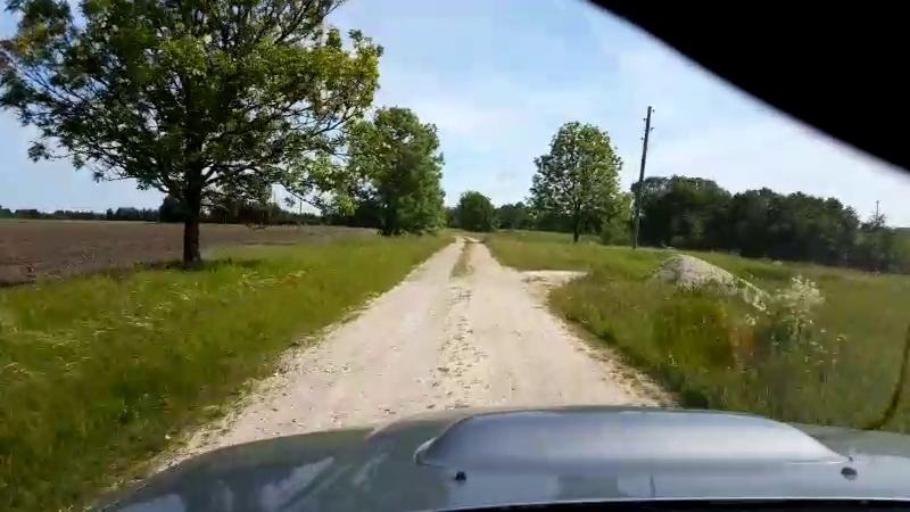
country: EE
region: Paernumaa
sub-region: Sauga vald
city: Sauga
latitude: 58.4946
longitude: 24.5362
